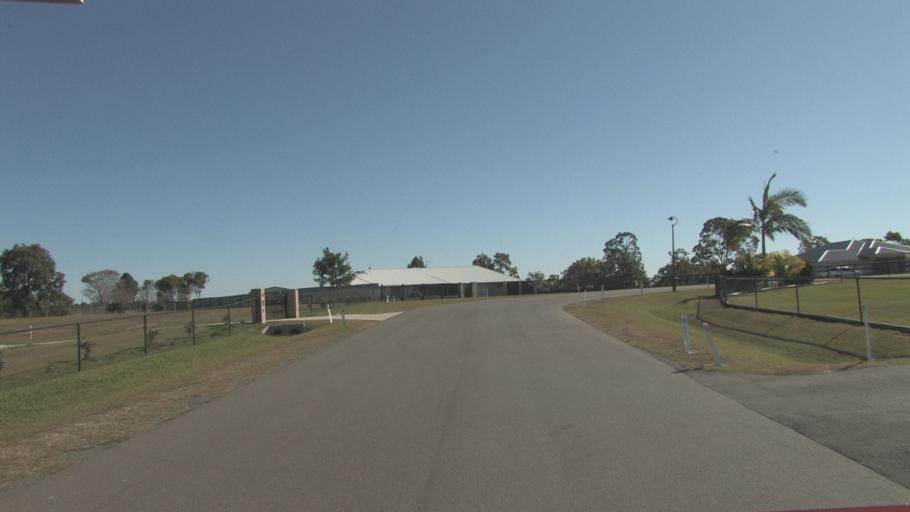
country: AU
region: Queensland
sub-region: Logan
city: Logan Reserve
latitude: -27.7270
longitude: 153.1233
